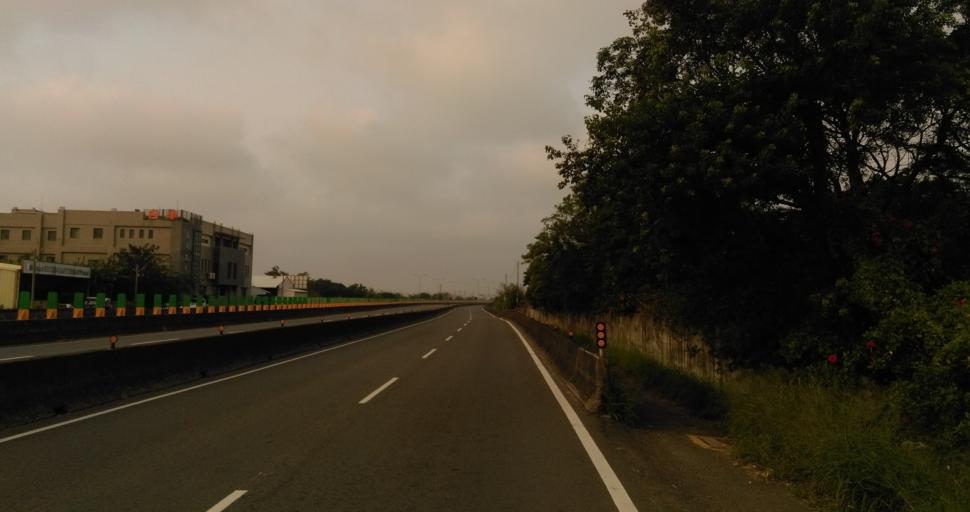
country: TW
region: Taiwan
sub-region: Hsinchu
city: Hsinchu
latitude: 24.7879
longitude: 120.9176
